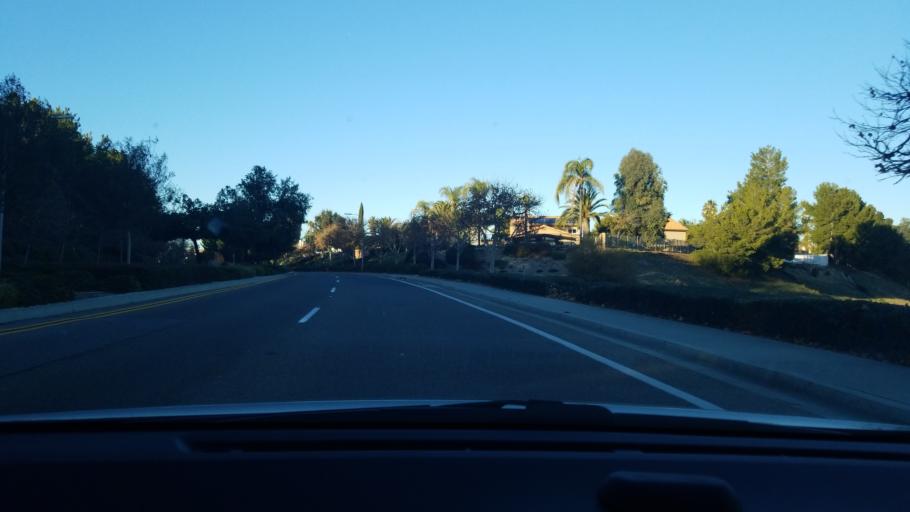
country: US
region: California
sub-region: Riverside County
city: Murrieta Hot Springs
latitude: 33.5388
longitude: -117.1501
